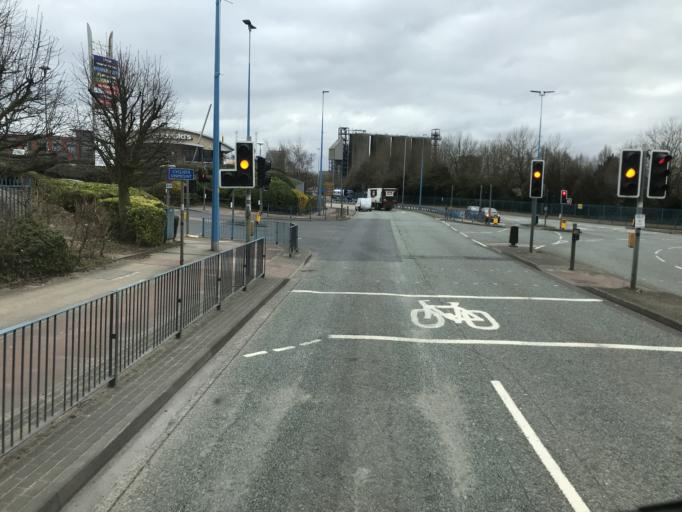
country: GB
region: England
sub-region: City and Borough of Salford
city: Eccles
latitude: 53.4824
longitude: -2.3306
